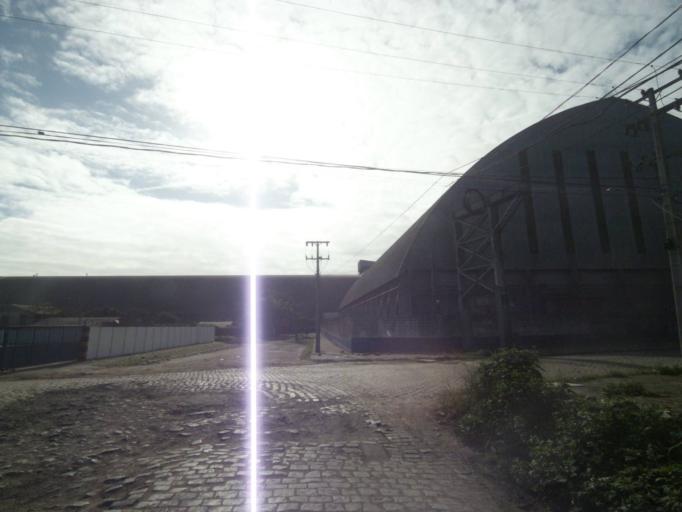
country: BR
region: Parana
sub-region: Paranagua
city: Paranagua
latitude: -25.5087
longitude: -48.5244
